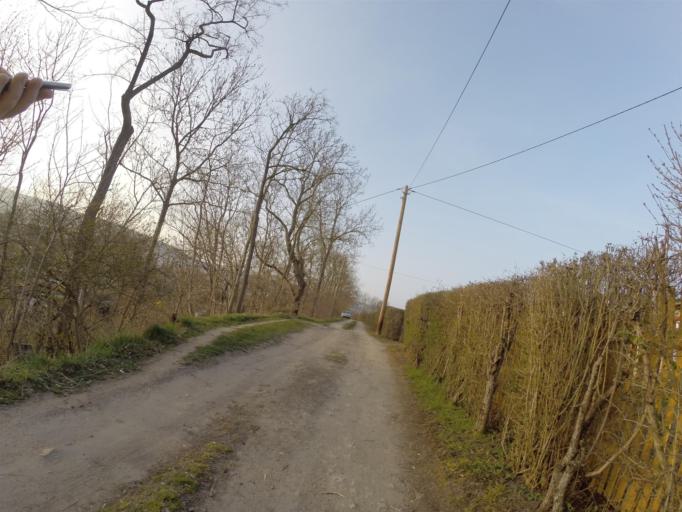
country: DE
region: Thuringia
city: Jena
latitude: 50.9363
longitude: 11.6095
